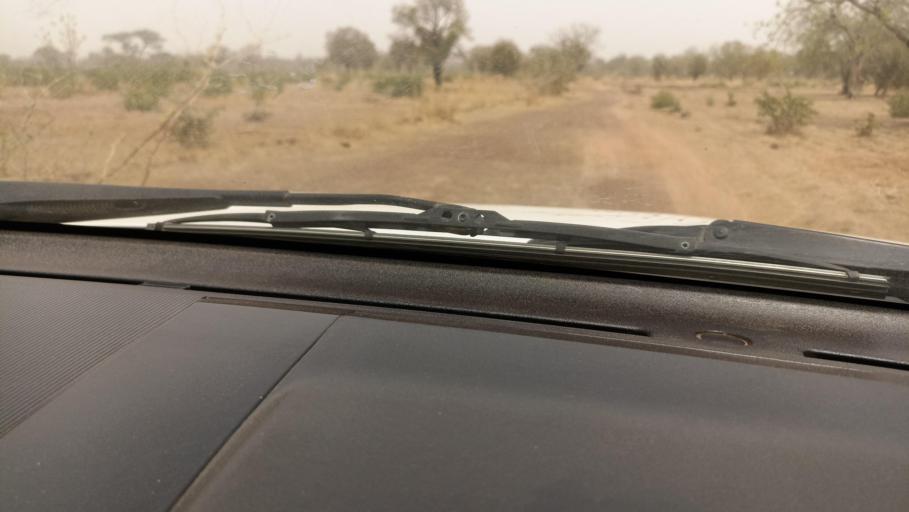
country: BF
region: Boucle du Mouhoun
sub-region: Province du Nayala
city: Toma
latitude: 12.8554
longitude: -2.8083
